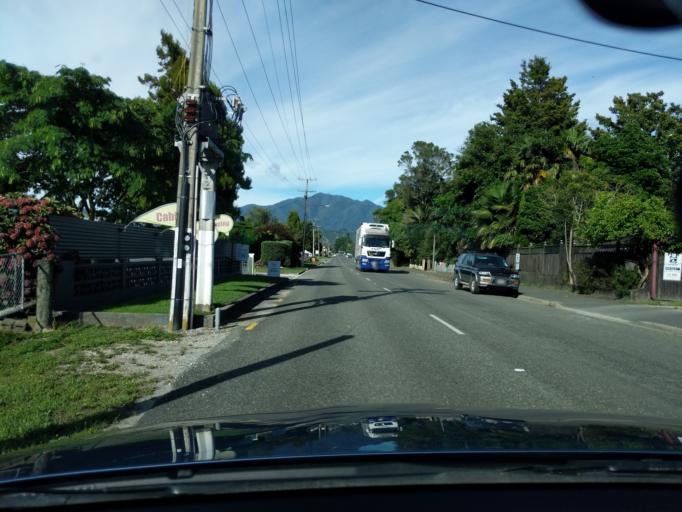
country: NZ
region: Tasman
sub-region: Tasman District
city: Takaka
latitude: -40.8579
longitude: 172.8106
